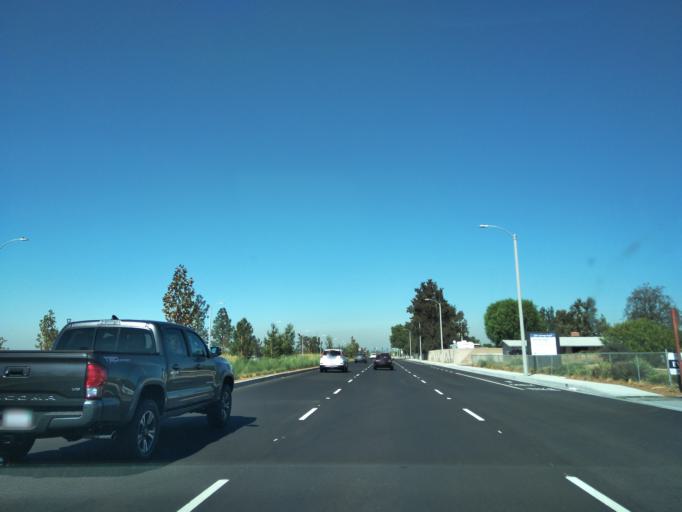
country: US
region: California
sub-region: Orange County
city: Lake Forest
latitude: 33.6877
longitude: -117.7225
